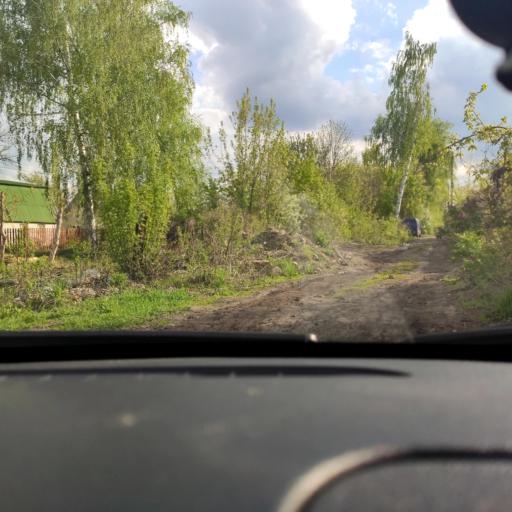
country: RU
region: Voronezj
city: Voronezh
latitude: 51.5996
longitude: 39.1554
